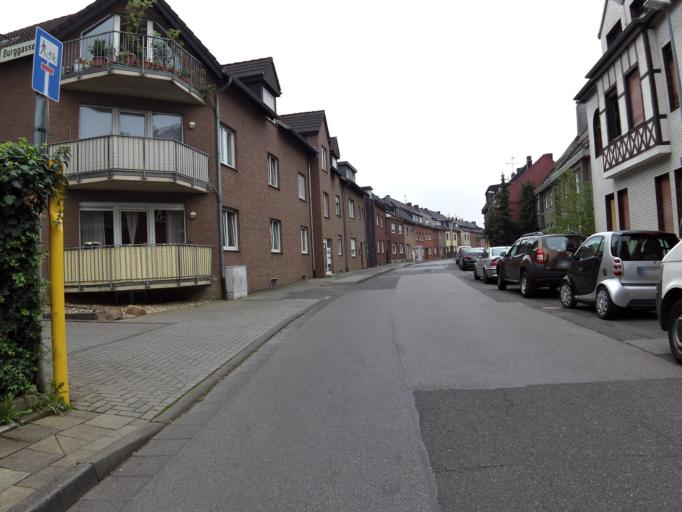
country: DE
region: North Rhine-Westphalia
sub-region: Regierungsbezirk Koln
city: Alsdorf
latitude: 50.8796
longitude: 6.1600
